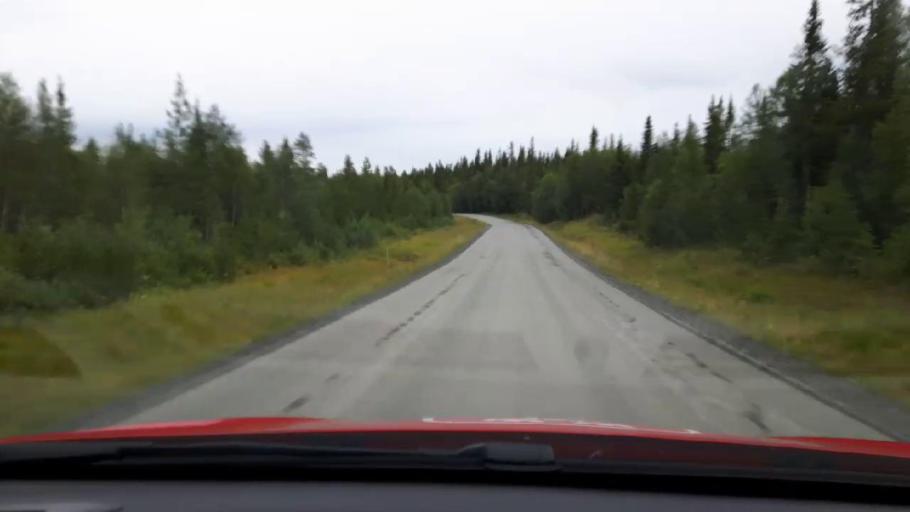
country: SE
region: Jaemtland
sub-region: Are Kommun
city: Are
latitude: 63.4537
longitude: 13.2057
